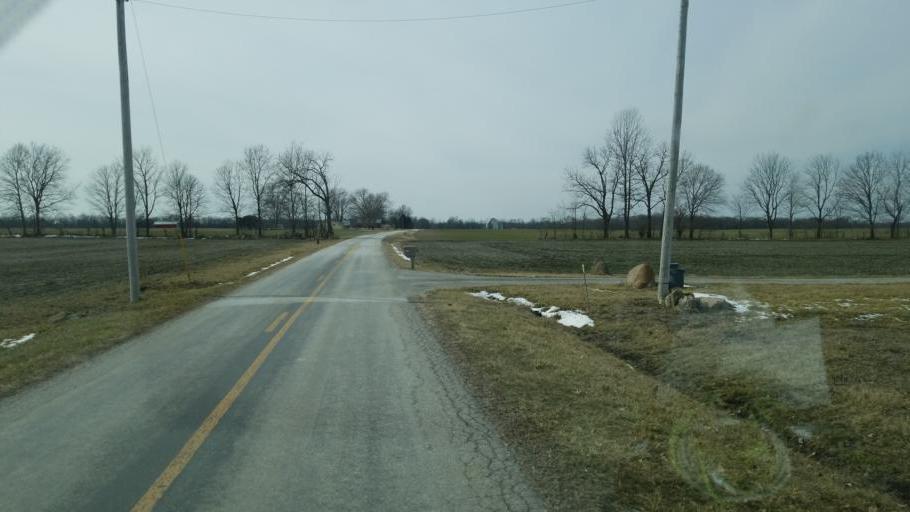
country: US
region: Ohio
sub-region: Marion County
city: Prospect
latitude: 40.3654
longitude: -83.1719
